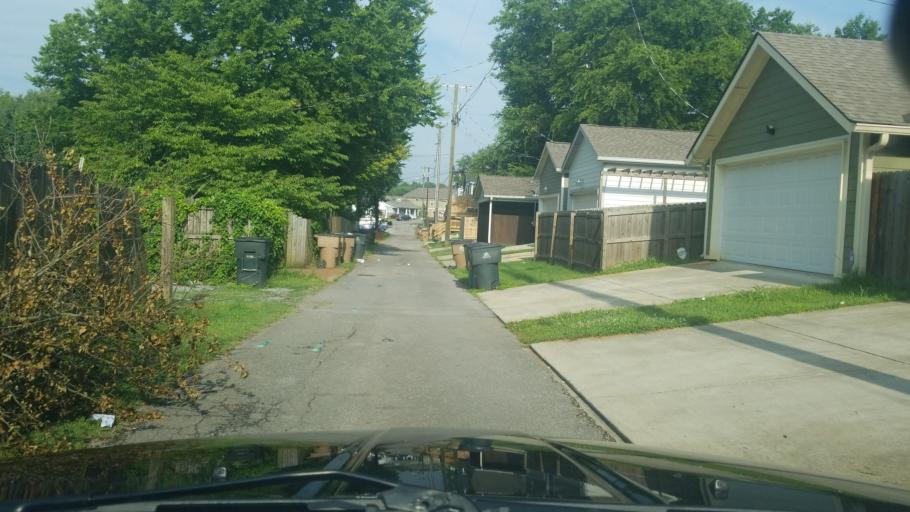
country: US
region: Tennessee
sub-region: Davidson County
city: Belle Meade
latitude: 36.1591
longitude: -86.8536
